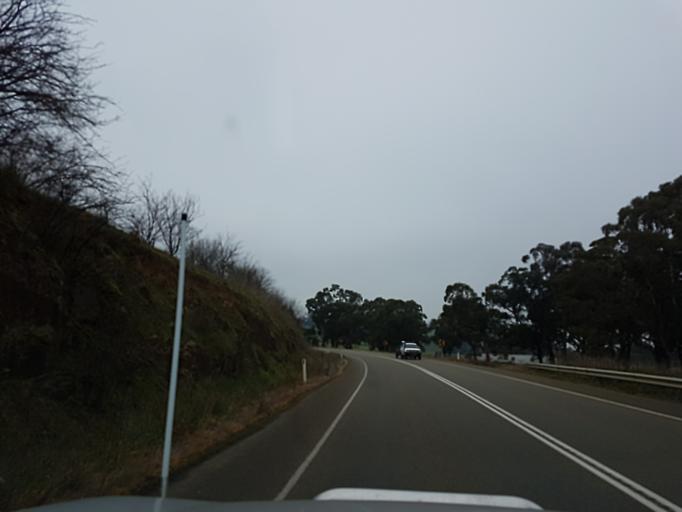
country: AU
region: Victoria
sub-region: Murrindindi
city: Alexandra
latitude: -37.2115
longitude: 145.4378
